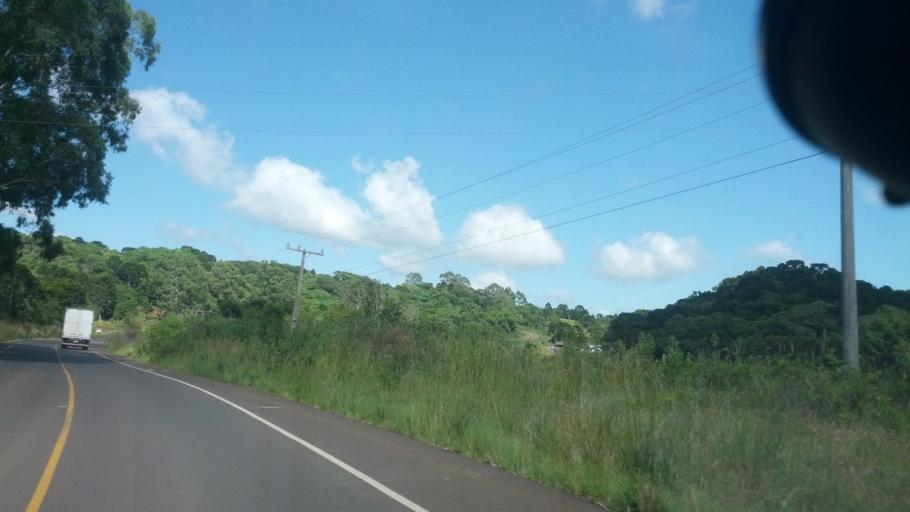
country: BR
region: Santa Catarina
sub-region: Lages
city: Lages
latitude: -27.9264
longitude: -50.5386
